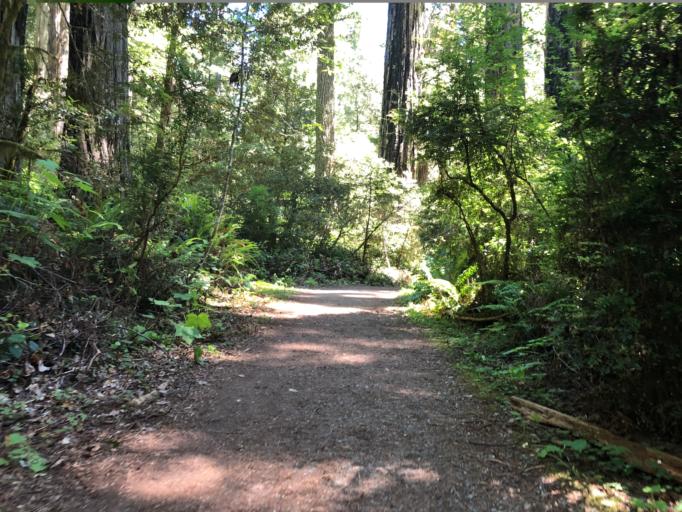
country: US
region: California
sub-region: Humboldt County
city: Westhaven-Moonstone
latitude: 41.3069
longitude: -124.0218
